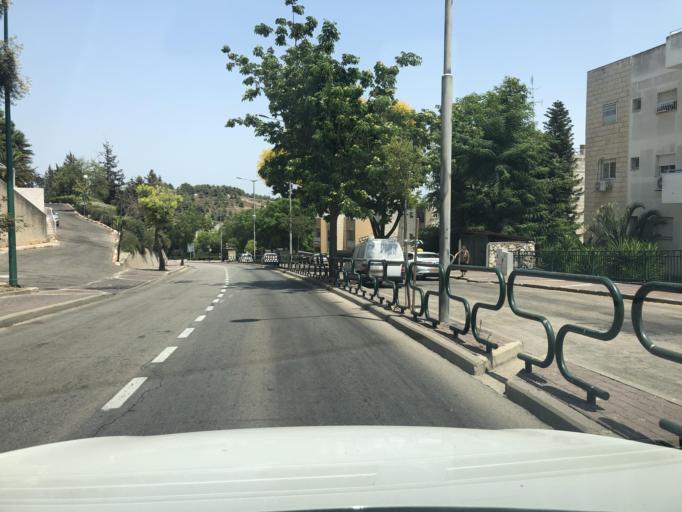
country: IL
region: Haifa
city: Daliyat el Karmil
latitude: 32.6523
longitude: 35.1011
